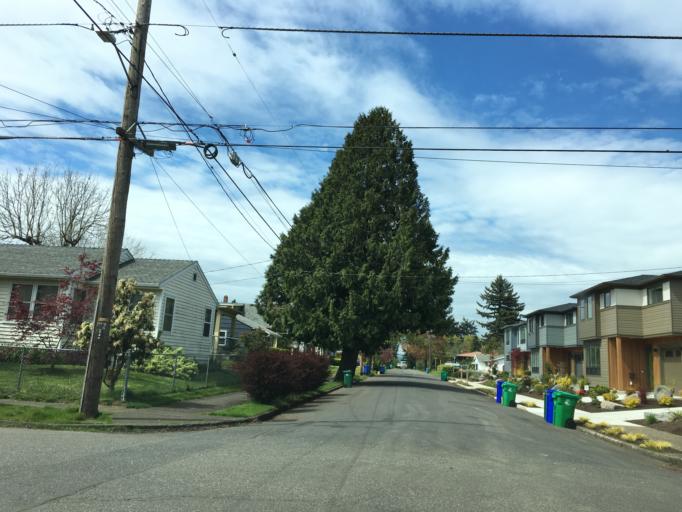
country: US
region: Oregon
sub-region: Multnomah County
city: Lents
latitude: 45.5304
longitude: -122.5897
